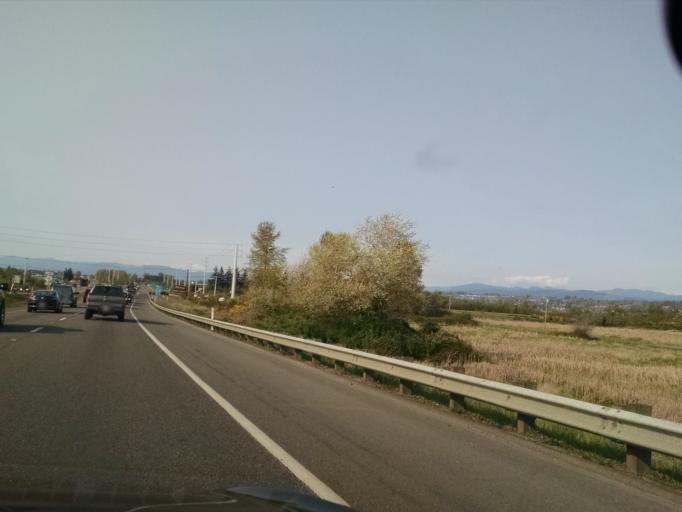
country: US
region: Washington
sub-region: Snohomish County
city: Marysville
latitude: 48.0204
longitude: -122.1866
